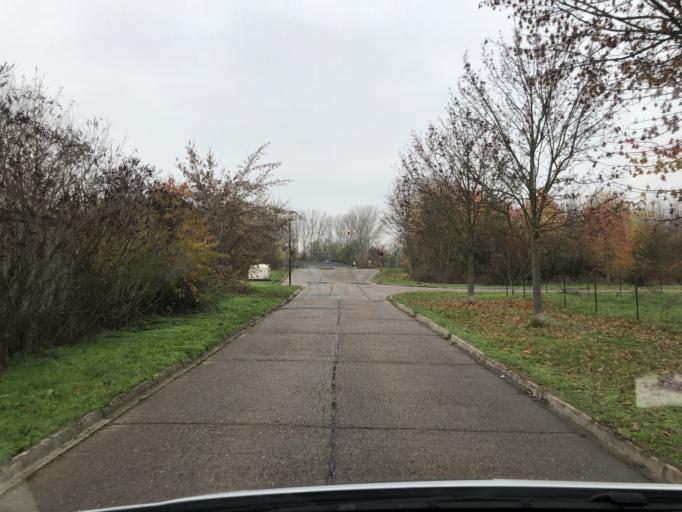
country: DE
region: Saxony-Anhalt
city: Halle Neustadt
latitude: 51.4666
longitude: 11.9212
